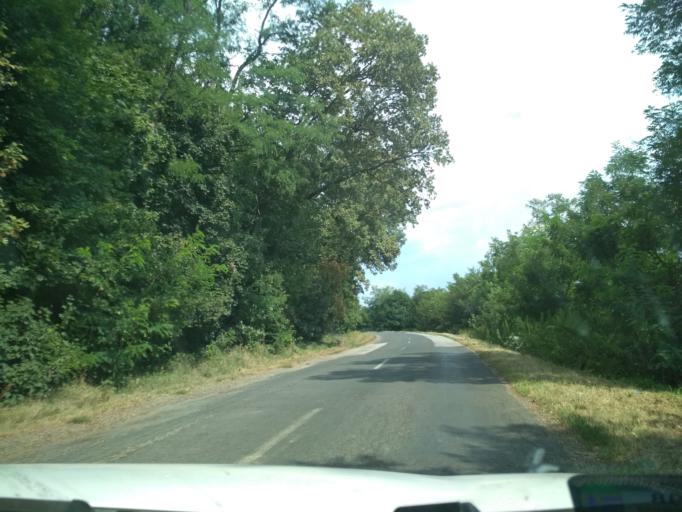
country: HU
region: Jasz-Nagykun-Szolnok
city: Tiszaszolos
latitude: 47.5205
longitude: 20.6625
